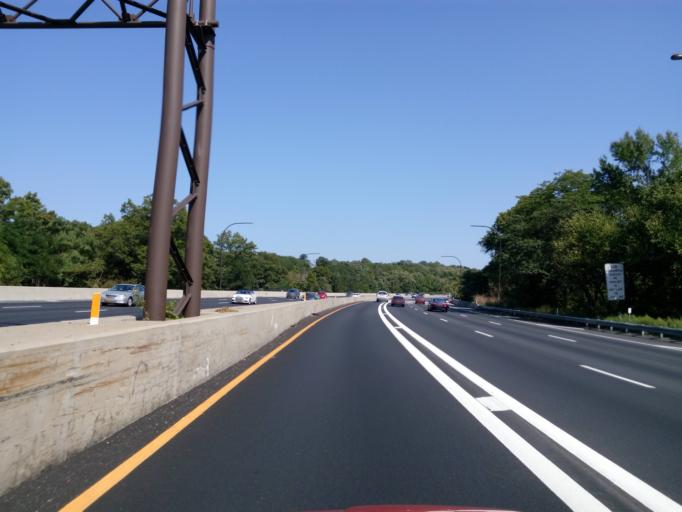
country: US
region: New York
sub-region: Nassau County
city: Old Westbury
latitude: 40.7836
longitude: -73.5909
